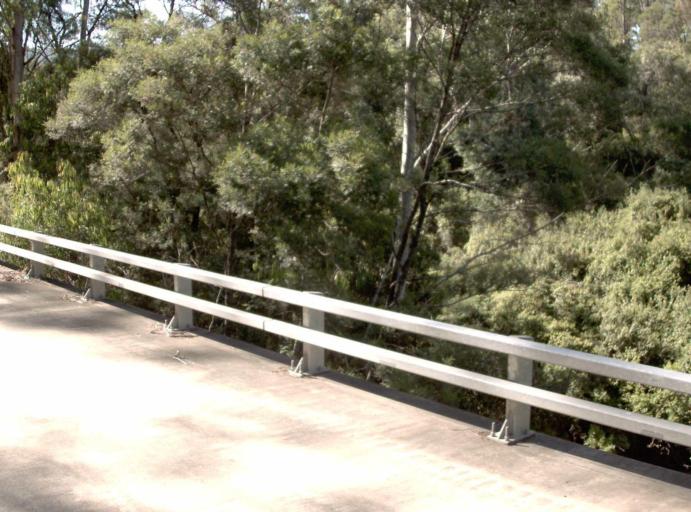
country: AU
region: Victoria
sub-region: East Gippsland
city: Lakes Entrance
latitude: -37.5043
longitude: 148.5382
